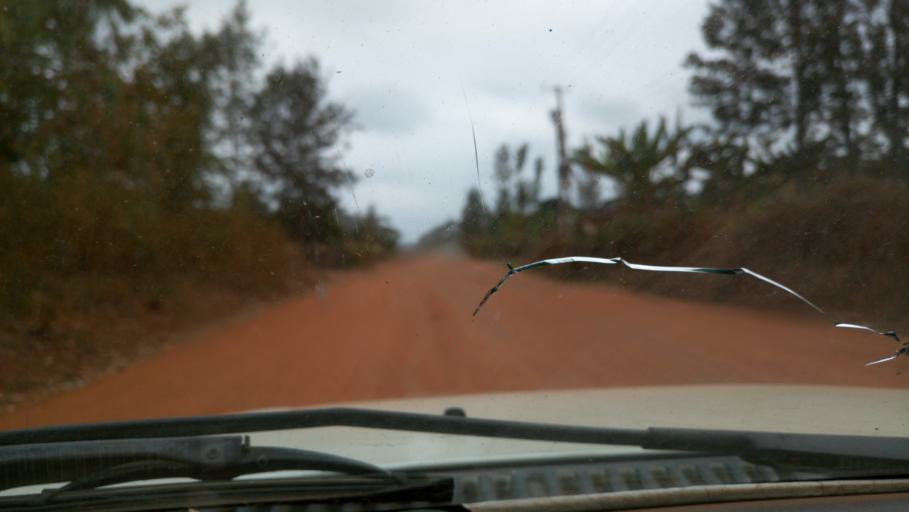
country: KE
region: Murang'a District
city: Maragua
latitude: -0.9528
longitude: 37.3172
